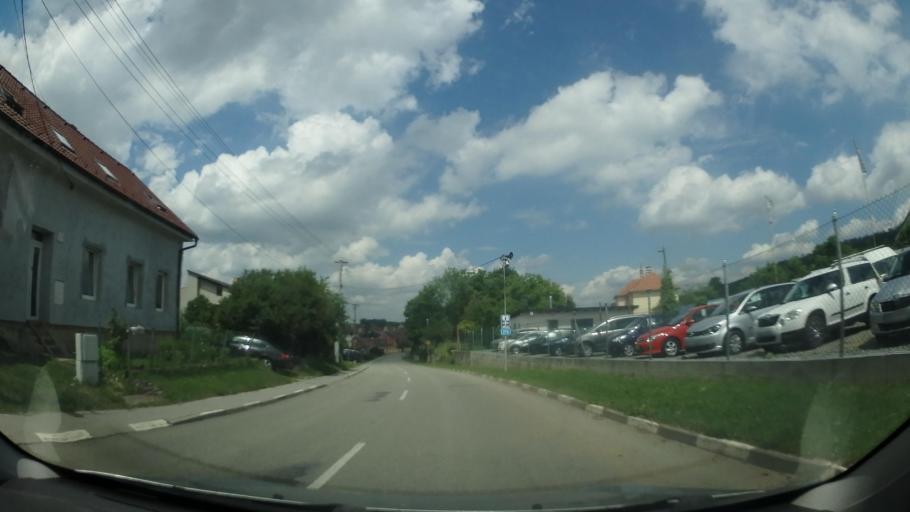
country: CZ
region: South Moravian
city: Velke Opatovice
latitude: 49.5461
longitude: 16.7086
